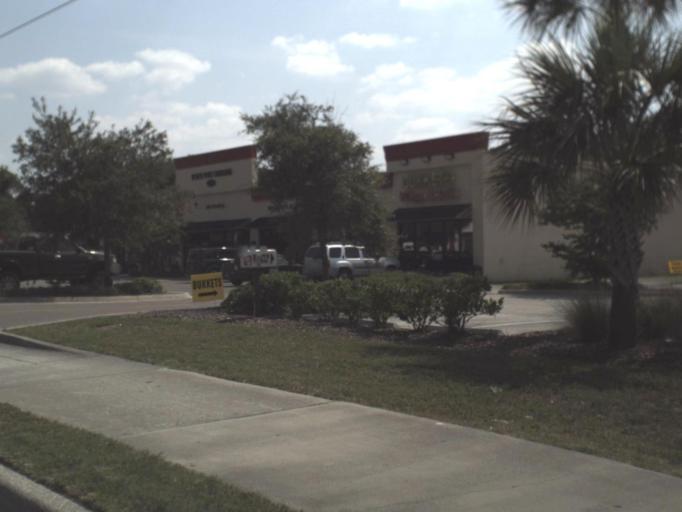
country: US
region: Florida
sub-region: Duval County
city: Atlantic Beach
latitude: 30.3464
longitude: -81.4135
